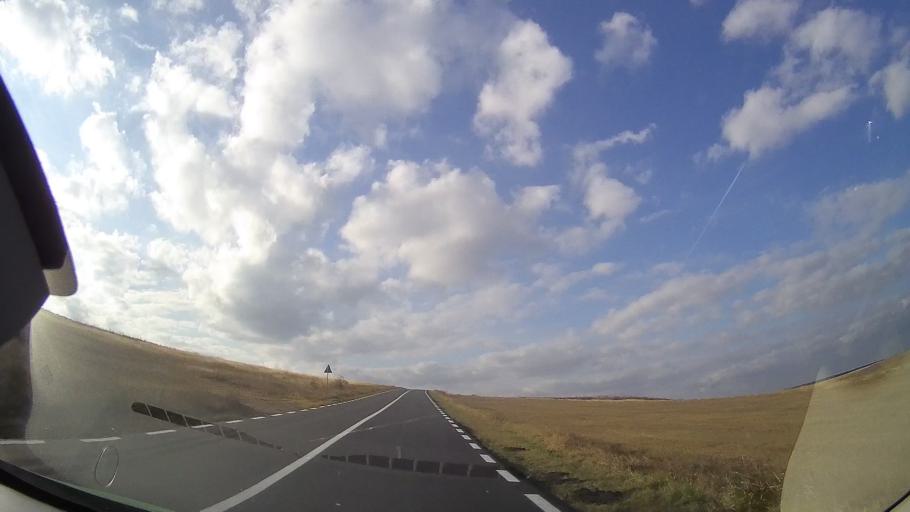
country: RO
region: Constanta
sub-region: Comuna Albesti
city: Albesti
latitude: 43.8084
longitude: 28.4174
